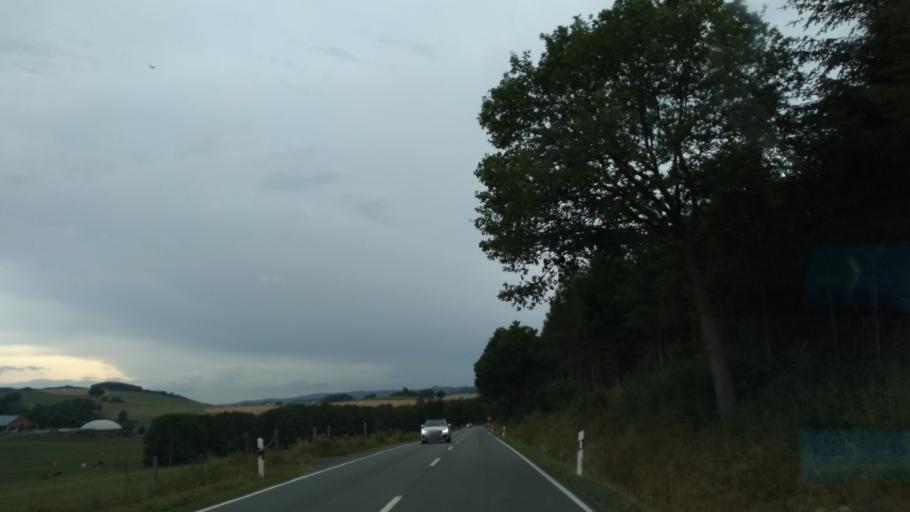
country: DE
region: North Rhine-Westphalia
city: Balve
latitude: 51.3047
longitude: 7.9098
